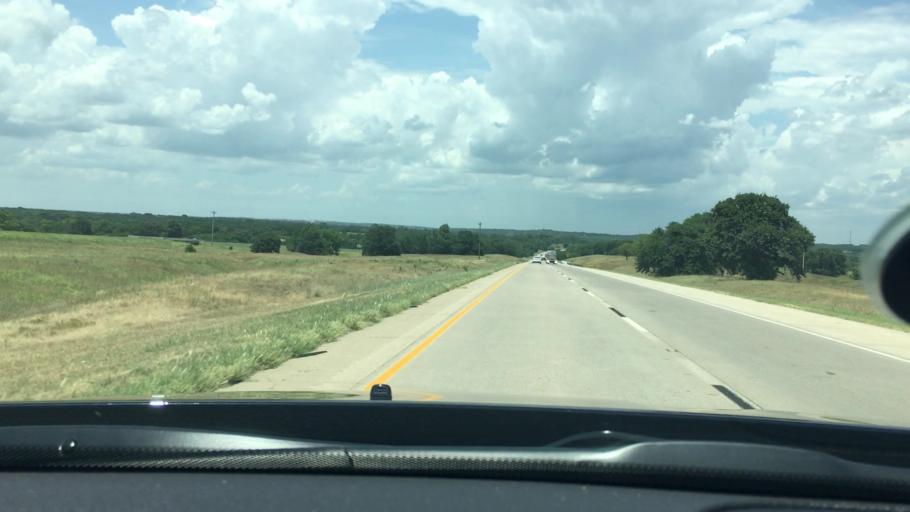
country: US
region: Oklahoma
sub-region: Love County
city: Marietta
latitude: 34.0251
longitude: -97.1467
